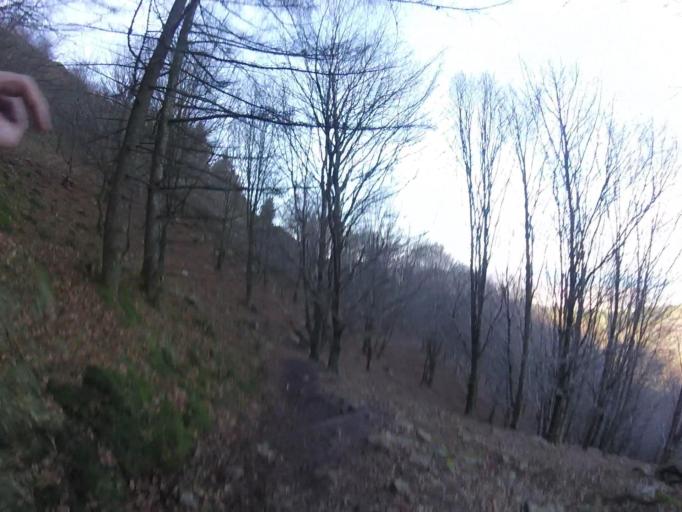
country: ES
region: Basque Country
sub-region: Provincia de Guipuzcoa
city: Irun
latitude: 43.2898
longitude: -1.7843
